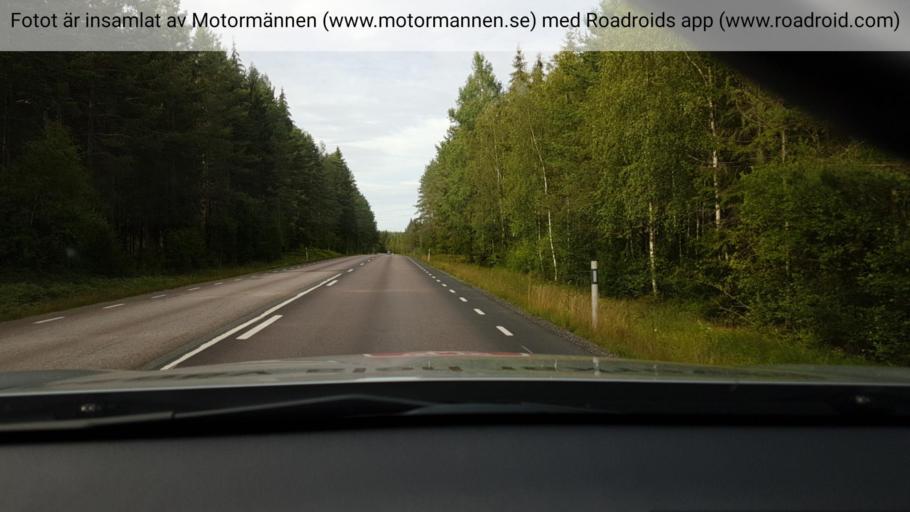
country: SE
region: Vaestra Goetaland
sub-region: Amals Kommun
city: Amal
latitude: 59.0631
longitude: 12.6534
